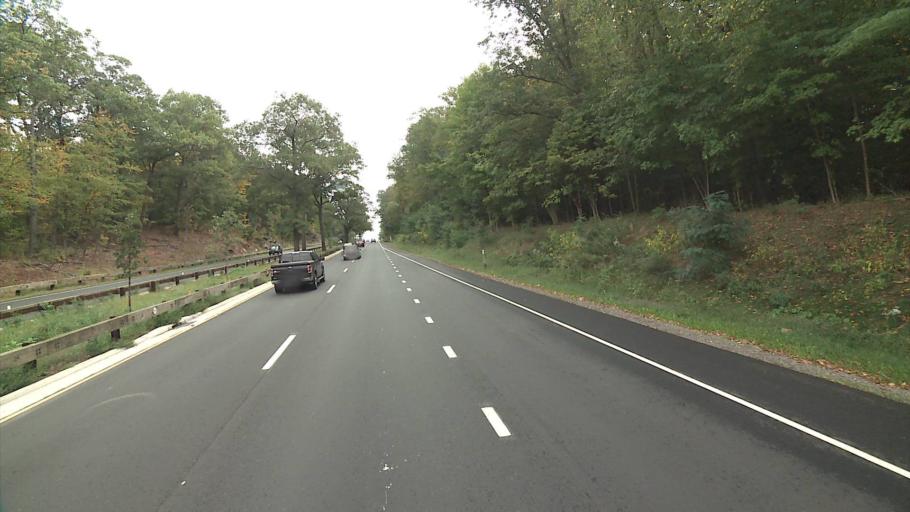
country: US
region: Connecticut
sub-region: Fairfield County
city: North Stamford
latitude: 41.1138
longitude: -73.5416
